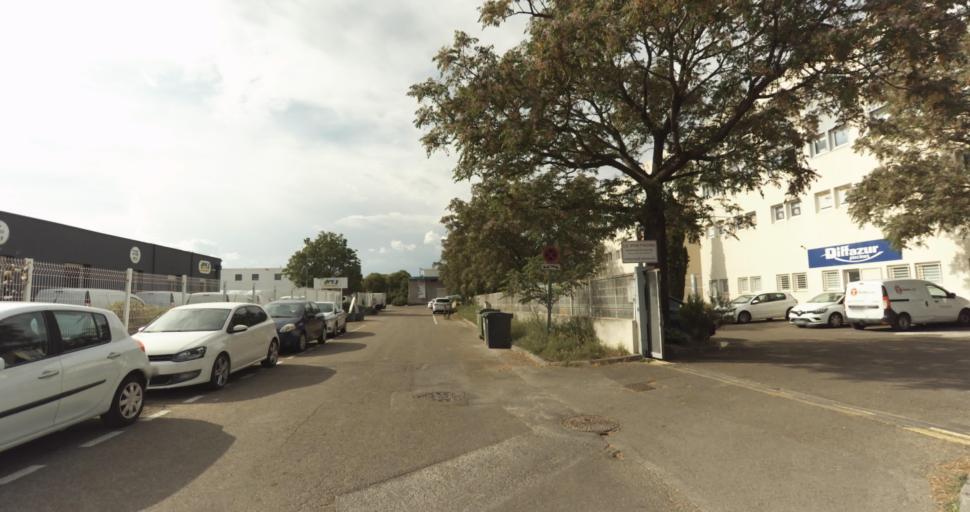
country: FR
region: Languedoc-Roussillon
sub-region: Departement du Gard
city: Nimes
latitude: 43.8161
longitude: 4.3349
